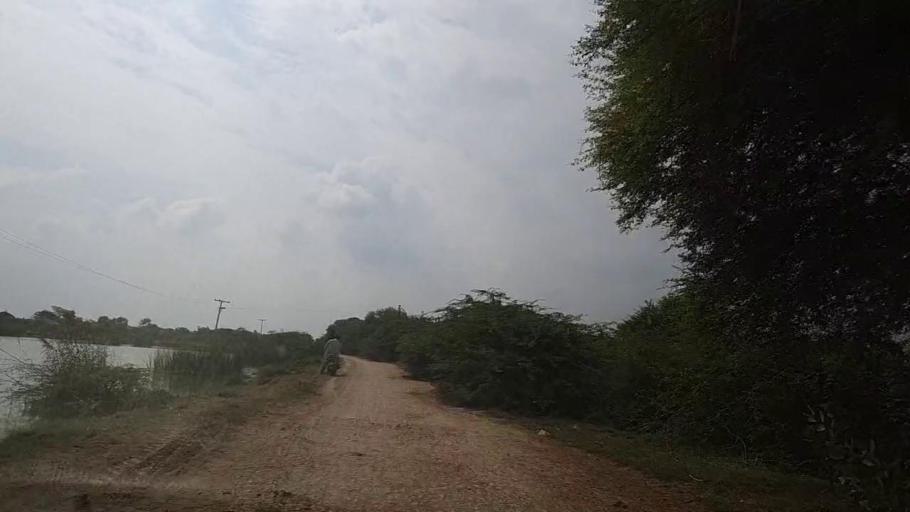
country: PK
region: Sindh
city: Mirpur Batoro
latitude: 24.5953
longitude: 68.1299
